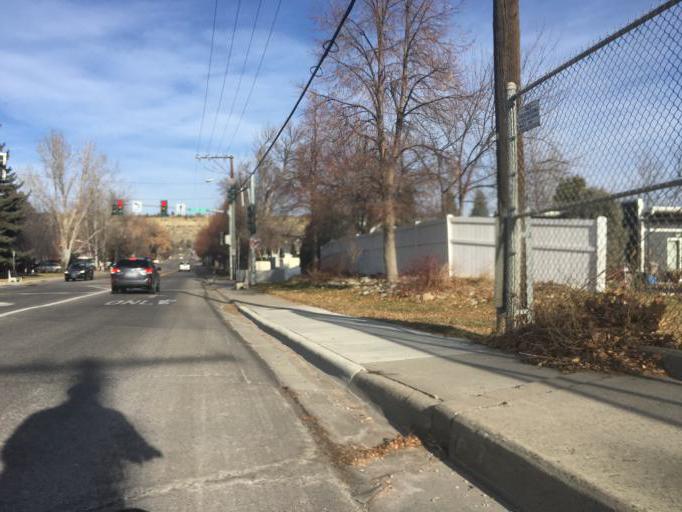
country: US
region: Montana
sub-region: Yellowstone County
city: Billings
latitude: 45.7909
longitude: -108.5590
